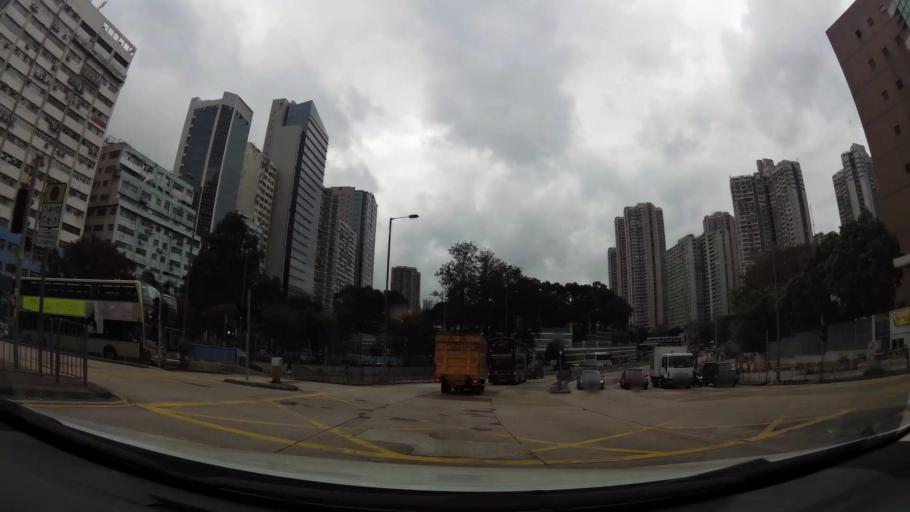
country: HK
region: Wong Tai Sin
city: Wong Tai Sin
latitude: 22.3397
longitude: 114.1981
